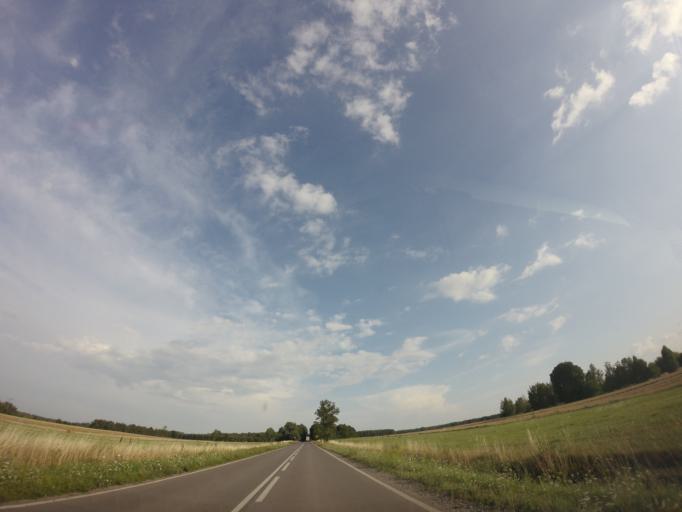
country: PL
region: Lublin Voivodeship
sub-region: Powiat lubartowski
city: Michow
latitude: 51.5467
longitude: 22.3005
